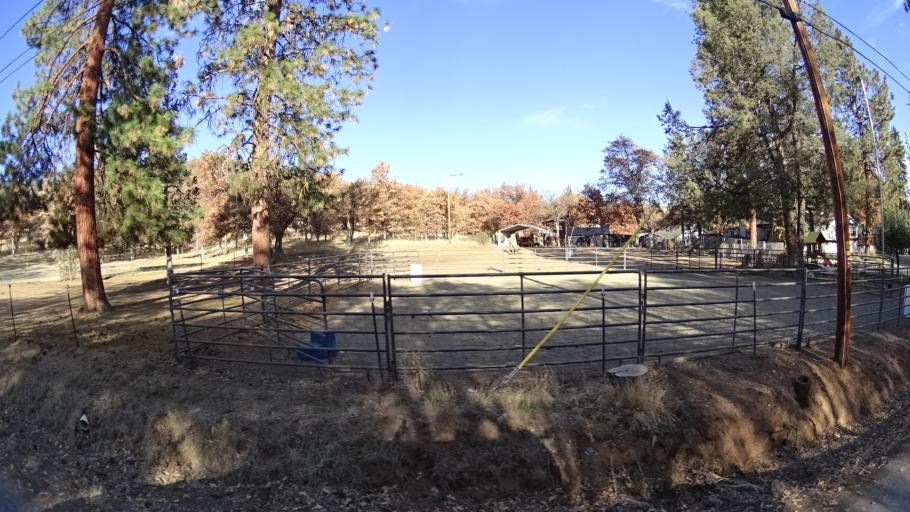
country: US
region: California
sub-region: Siskiyou County
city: Yreka
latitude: 41.6822
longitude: -122.6410
